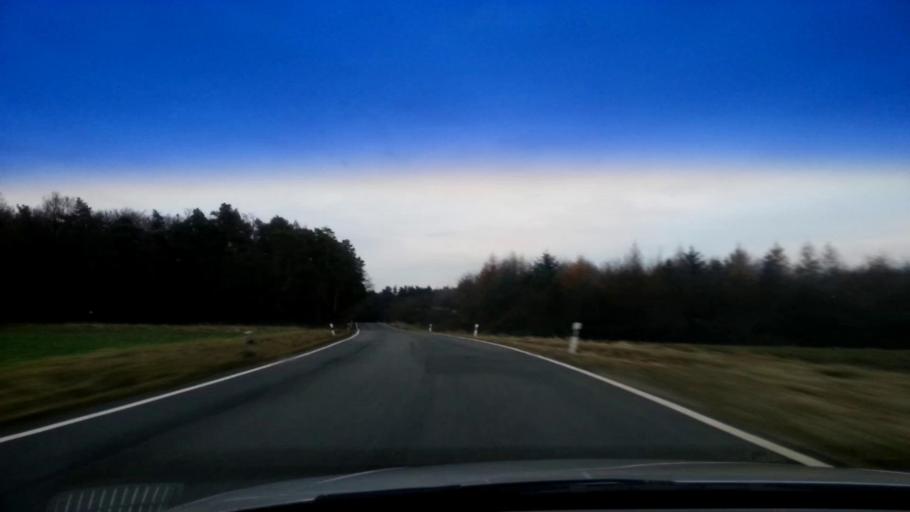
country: DE
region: Bavaria
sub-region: Regierungsbezirk Mittelfranken
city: Muhlhausen
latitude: 49.7969
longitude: 10.7845
